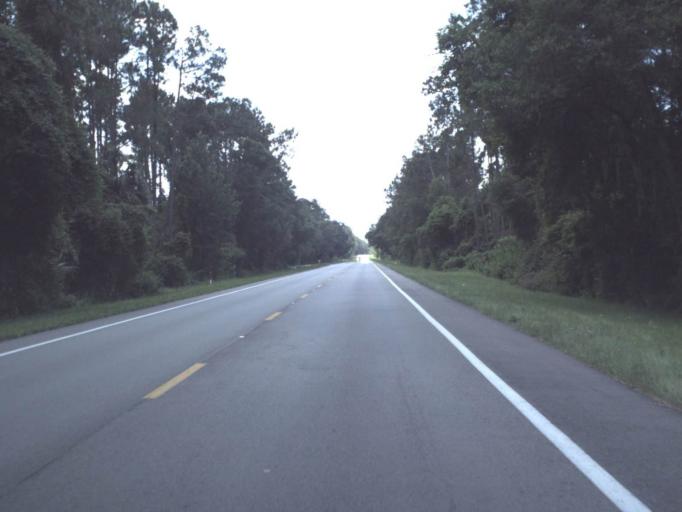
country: US
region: Florida
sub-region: Putnam County
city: Crescent City
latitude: 29.3986
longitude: -81.5092
